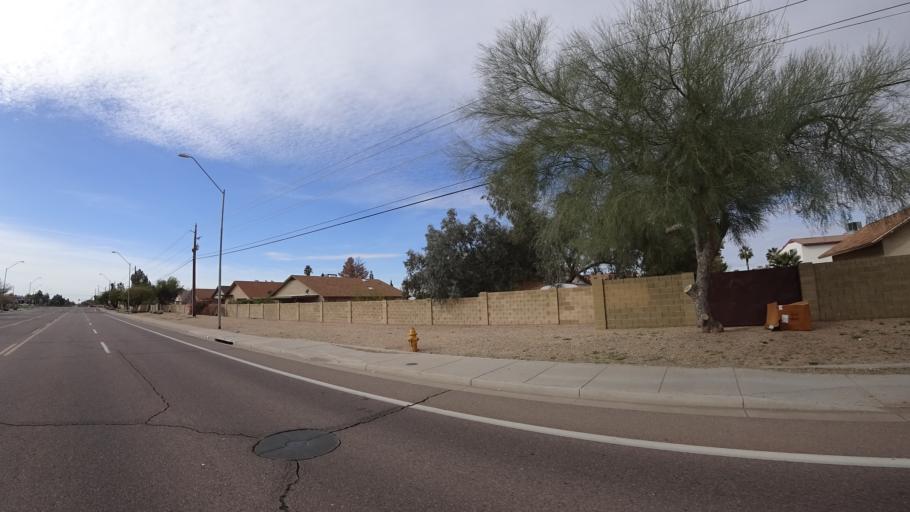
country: US
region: Arizona
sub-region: Maricopa County
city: Peoria
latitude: 33.6583
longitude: -112.1520
